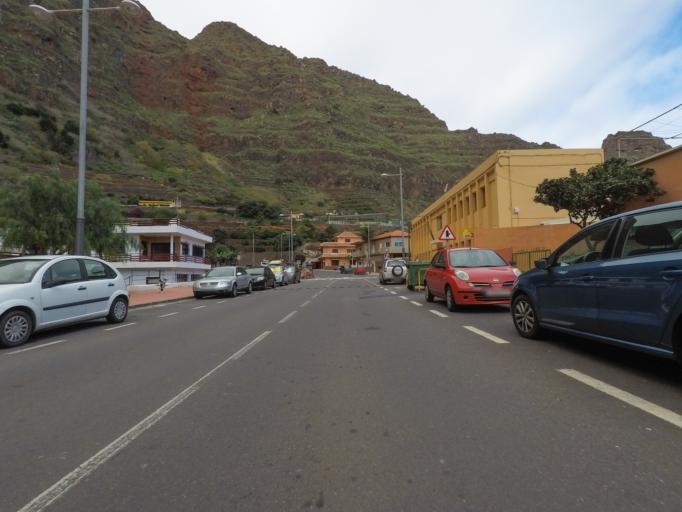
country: ES
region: Canary Islands
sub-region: Provincia de Santa Cruz de Tenerife
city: Agulo
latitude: 28.1865
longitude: -17.1955
